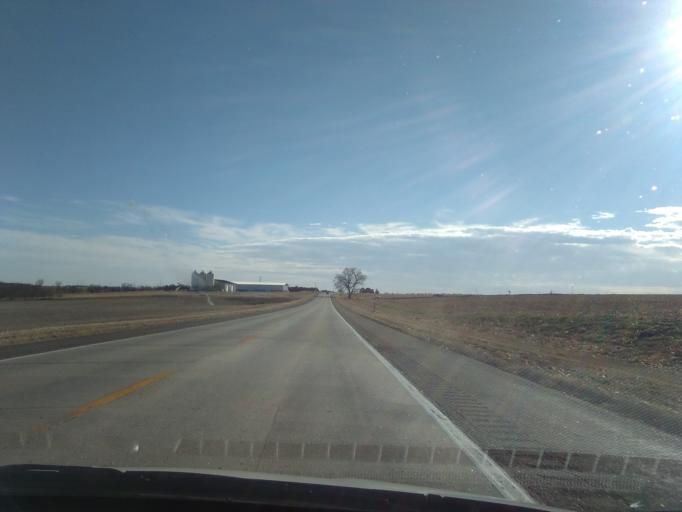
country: US
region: Nebraska
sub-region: Adams County
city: Hastings
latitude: 40.3607
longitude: -98.4397
